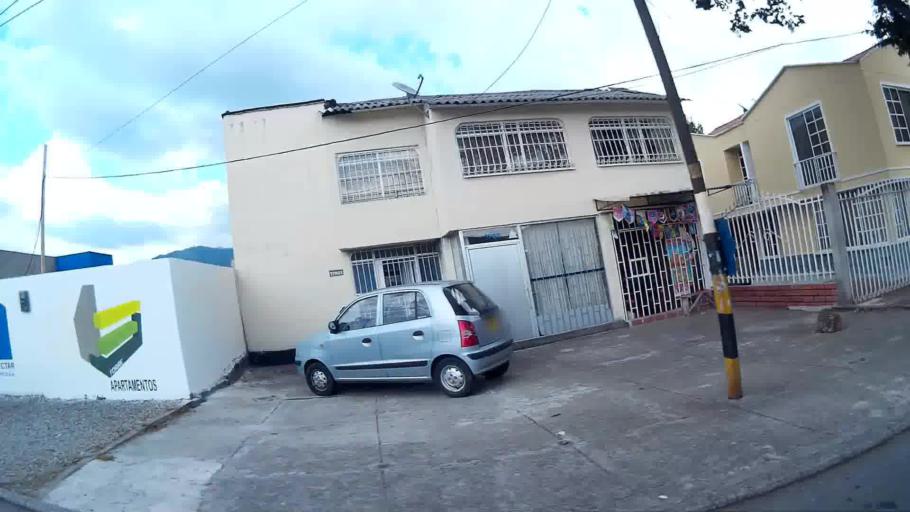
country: CO
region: Quindio
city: Calarca
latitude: 4.5671
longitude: -75.6482
